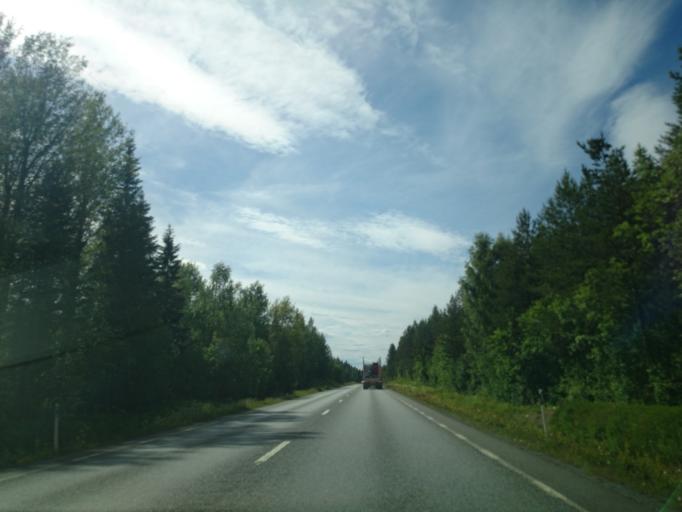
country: SE
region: Jaemtland
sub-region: Krokoms Kommun
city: Krokom
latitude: 63.3214
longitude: 14.2440
